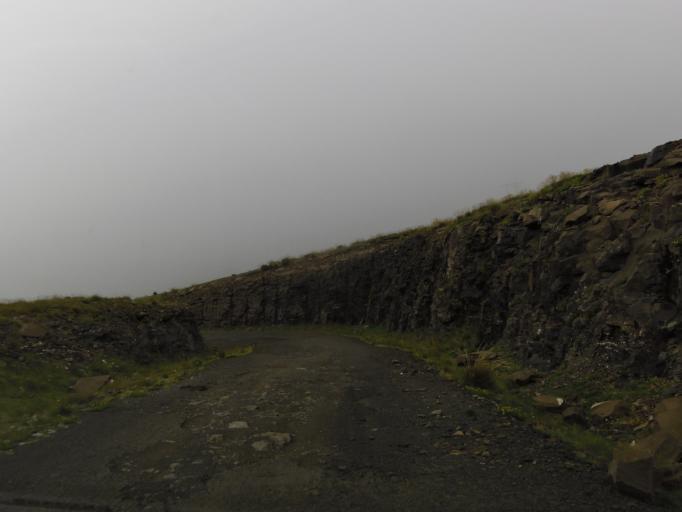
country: LS
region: Butha-Buthe
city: Butha-Buthe
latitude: -29.0651
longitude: 28.4058
